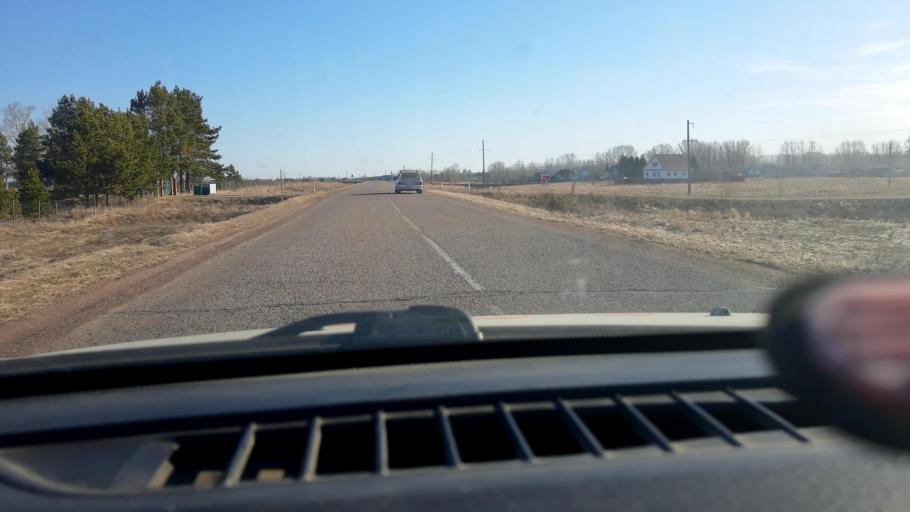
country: RU
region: Bashkortostan
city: Asanovo
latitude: 54.9242
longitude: 55.5144
